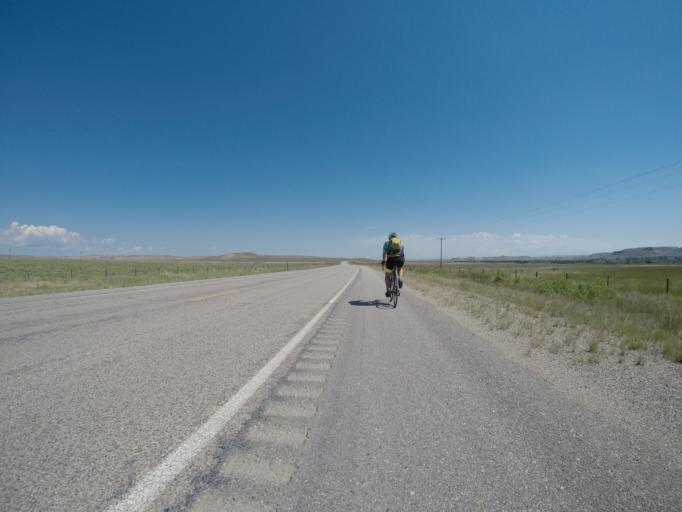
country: US
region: Wyoming
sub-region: Sublette County
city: Marbleton
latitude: 42.4198
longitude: -110.1126
